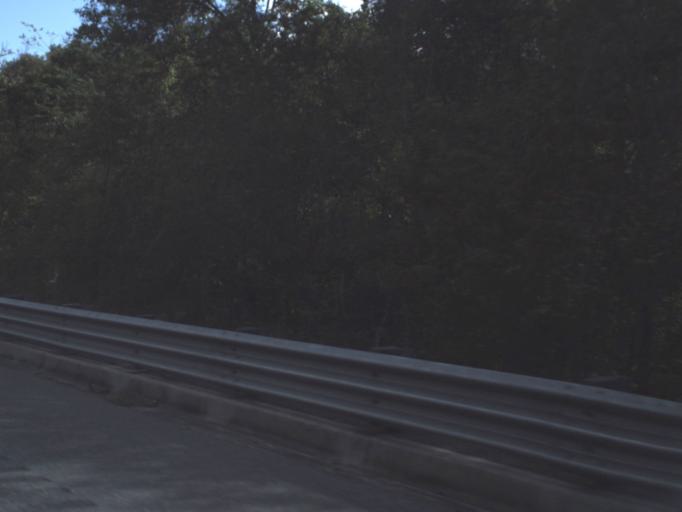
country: US
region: Florida
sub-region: Sumter County
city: Wildwood
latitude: 28.8546
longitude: -82.0884
